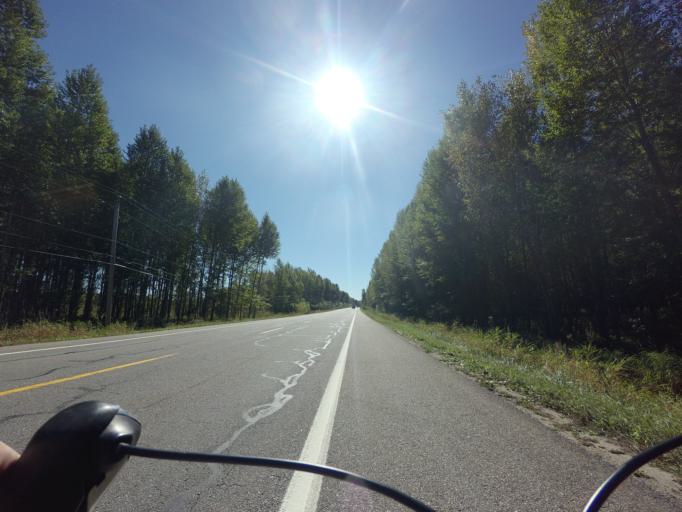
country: CA
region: Ontario
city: Clarence-Rockland
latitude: 45.5380
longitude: -75.4143
